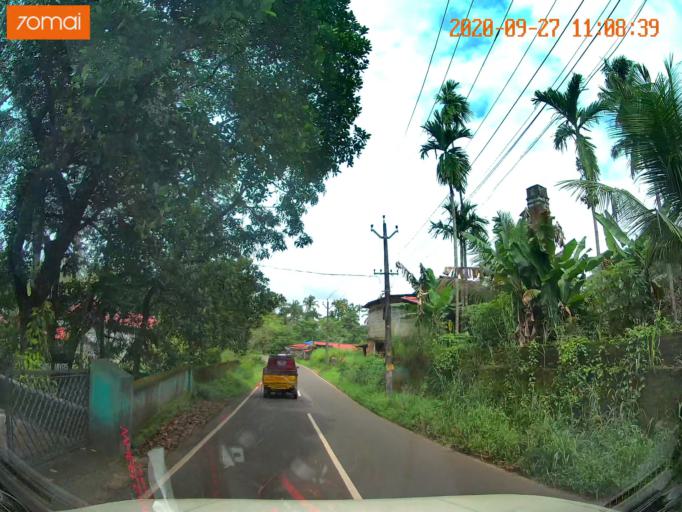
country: IN
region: Kerala
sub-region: Thrissur District
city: Trichur
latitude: 10.4314
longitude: 76.2323
